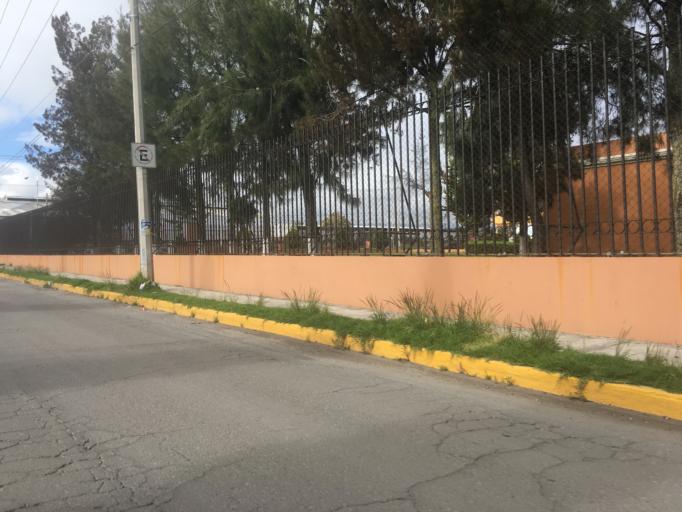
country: MX
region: Mexico
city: Santa Maria Totoltepec
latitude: 19.2969
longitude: -99.5941
